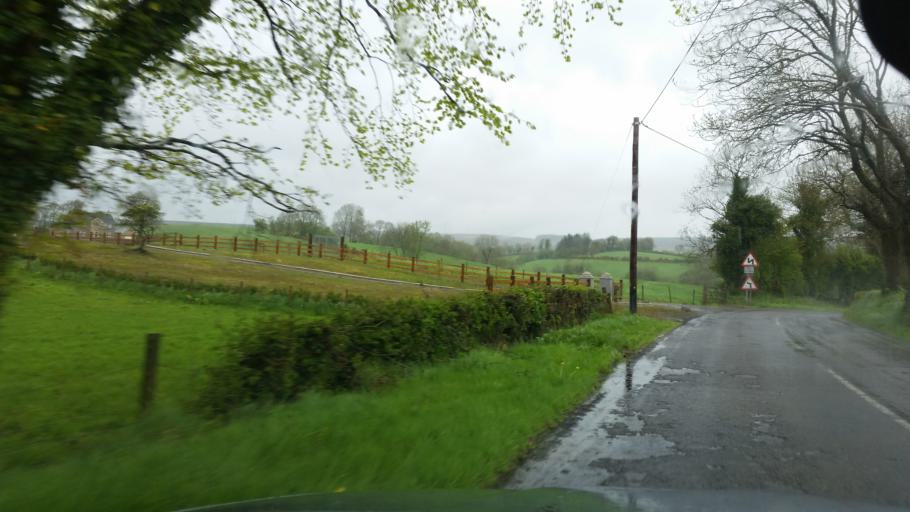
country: GB
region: Northern Ireland
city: Fivemiletown
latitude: 54.4093
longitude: -7.3205
